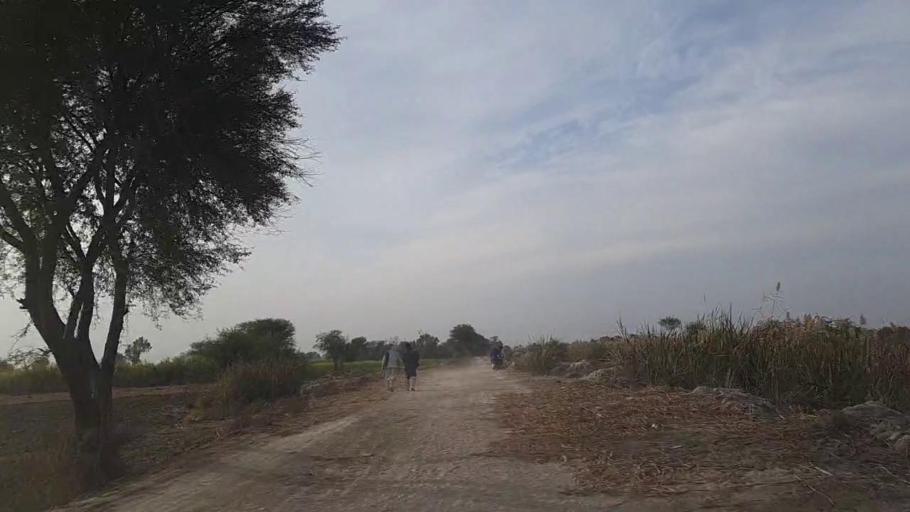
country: PK
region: Sindh
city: Daur
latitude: 26.5266
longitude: 68.4061
